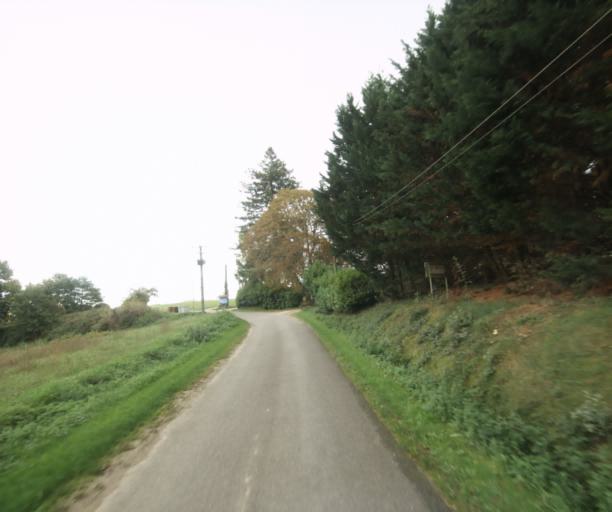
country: FR
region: Midi-Pyrenees
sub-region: Departement du Gers
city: Eauze
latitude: 43.8940
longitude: 0.1207
